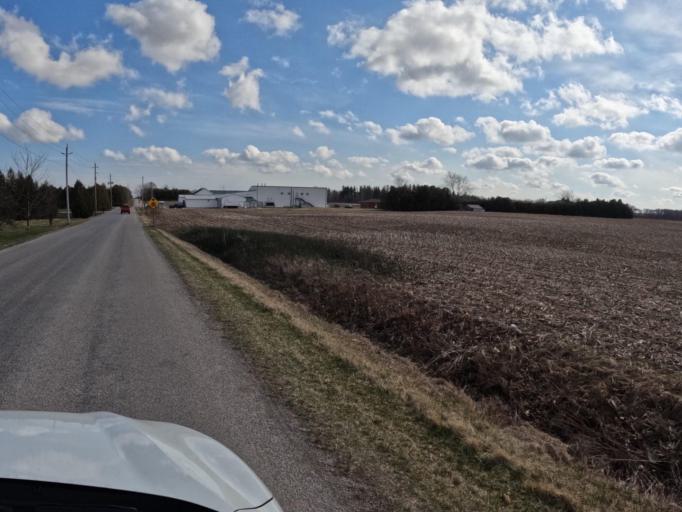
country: CA
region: Ontario
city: Norfolk County
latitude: 42.8655
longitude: -80.2758
